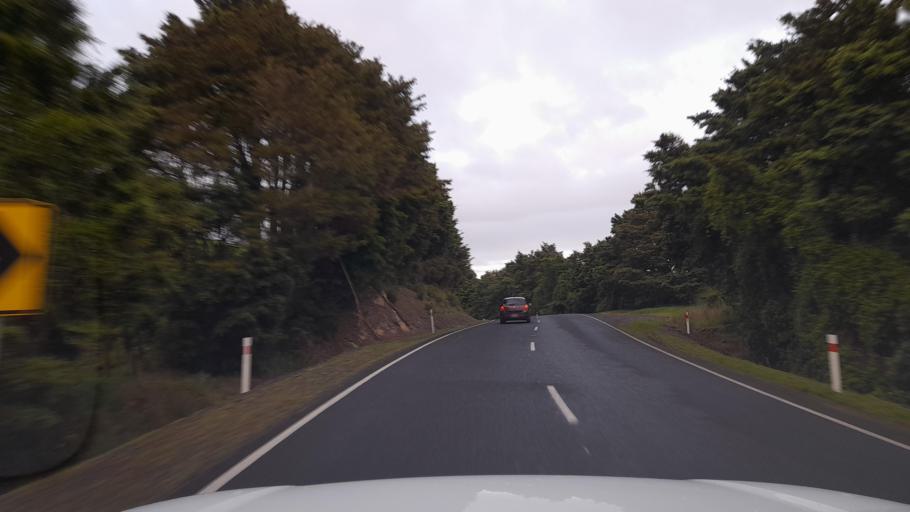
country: NZ
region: Northland
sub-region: Whangarei
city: Maungatapere
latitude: -35.7081
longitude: 174.0081
